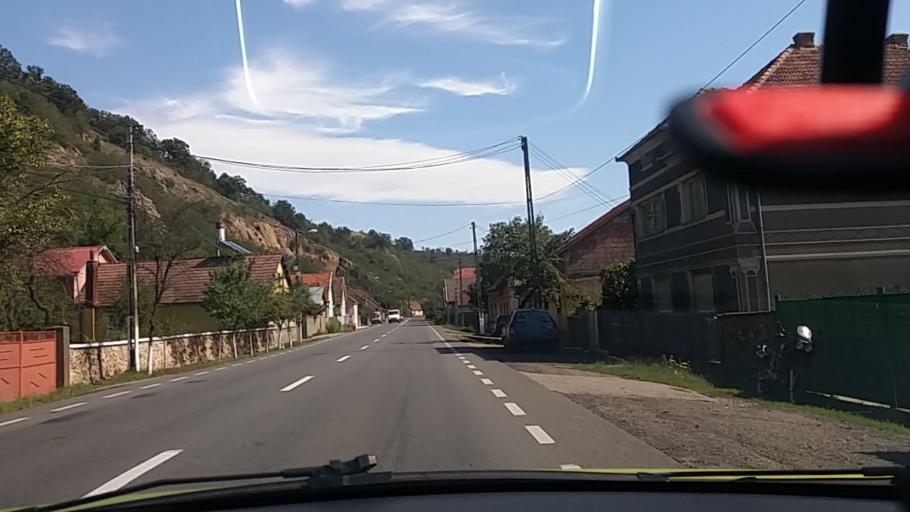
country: RO
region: Arad
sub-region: Oras Lipova
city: Lipova
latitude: 46.1014
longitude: 21.6968
